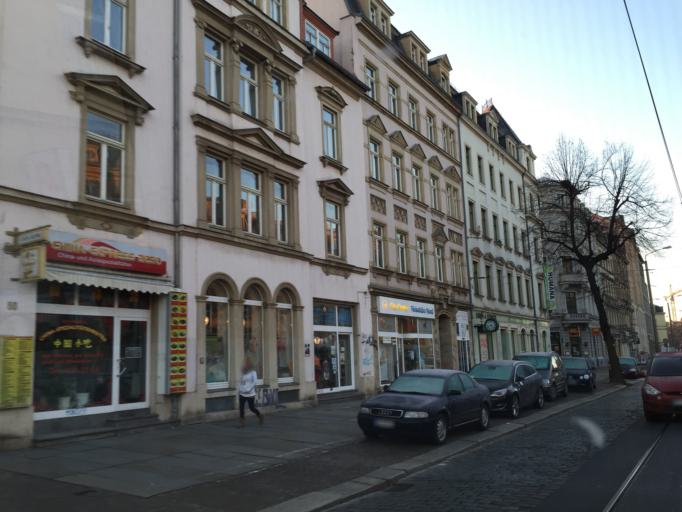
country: DE
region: Saxony
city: Dresden
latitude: 51.0695
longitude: 13.7491
